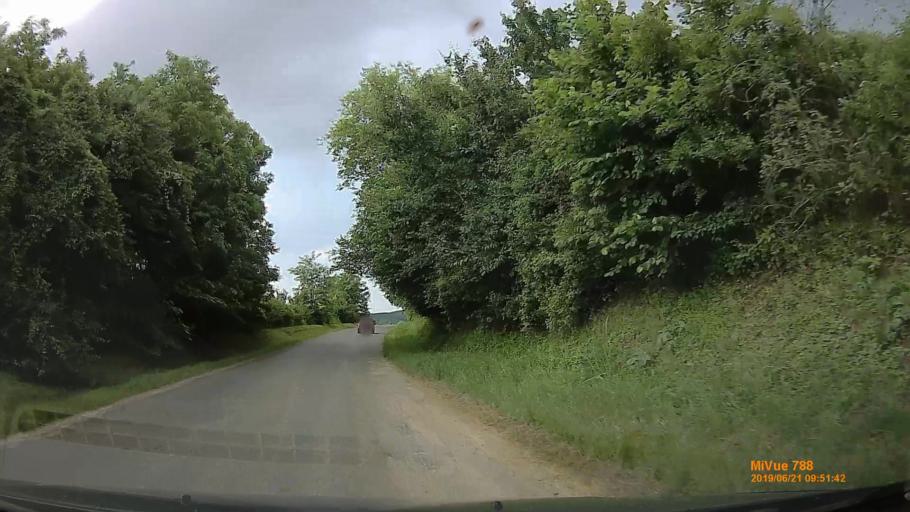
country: HU
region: Baranya
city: Sasd
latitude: 46.2493
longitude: 18.0208
